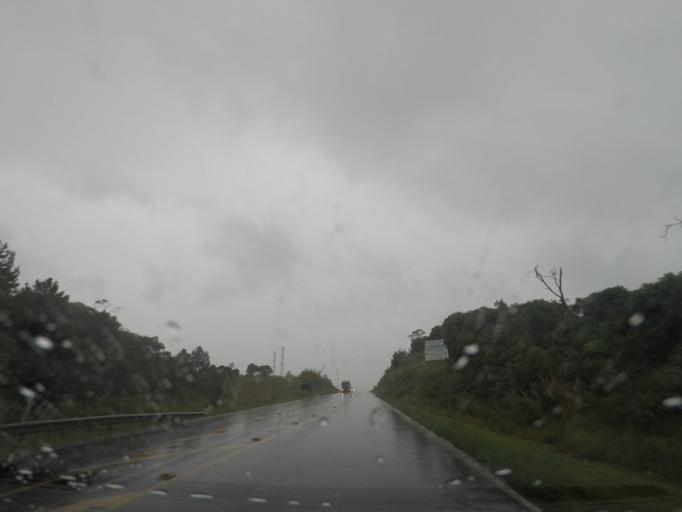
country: BR
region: Parana
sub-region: Almirante Tamandare
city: Almirante Tamandare
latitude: -25.3534
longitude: -49.3016
